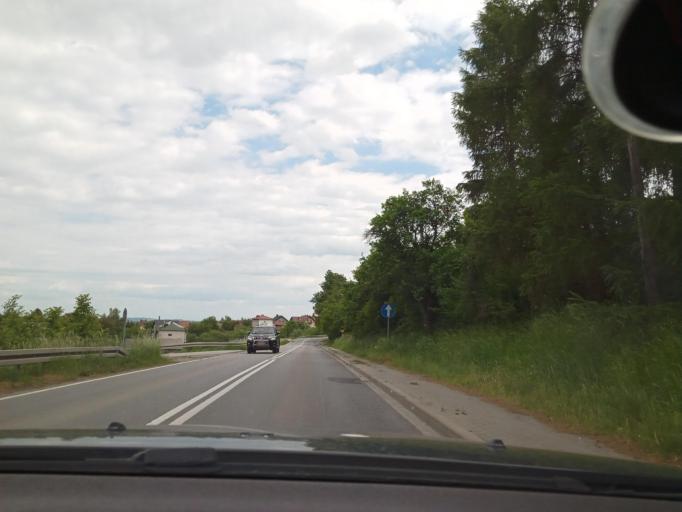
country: PL
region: Lesser Poland Voivodeship
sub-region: Powiat wielicki
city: Trabki
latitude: 49.9539
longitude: 20.1578
